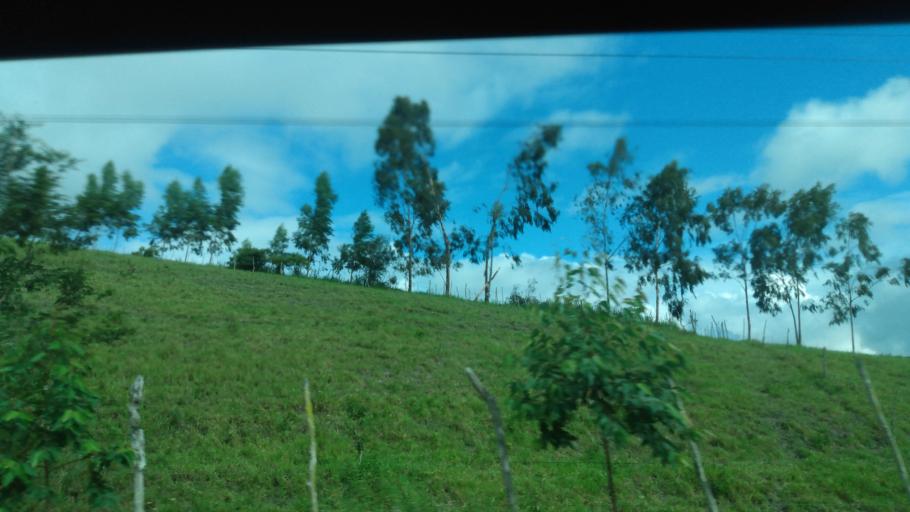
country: BR
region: Pernambuco
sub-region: Quipapa
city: Quipapa
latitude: -8.7806
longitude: -35.9363
